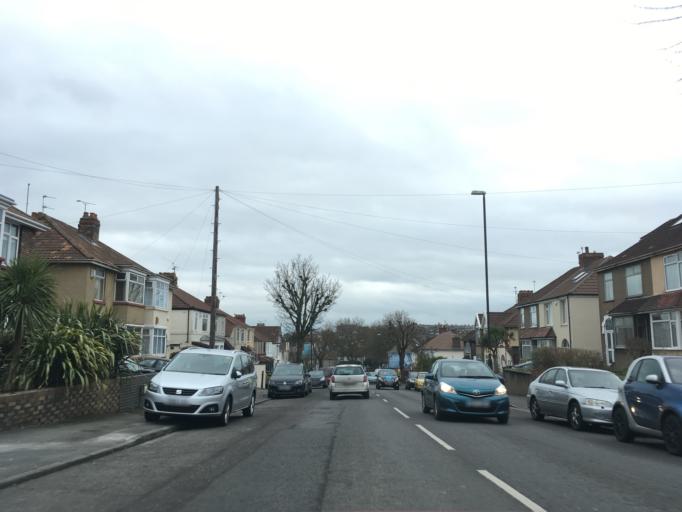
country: GB
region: England
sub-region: Bristol
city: Bristol
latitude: 51.4845
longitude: -2.5795
